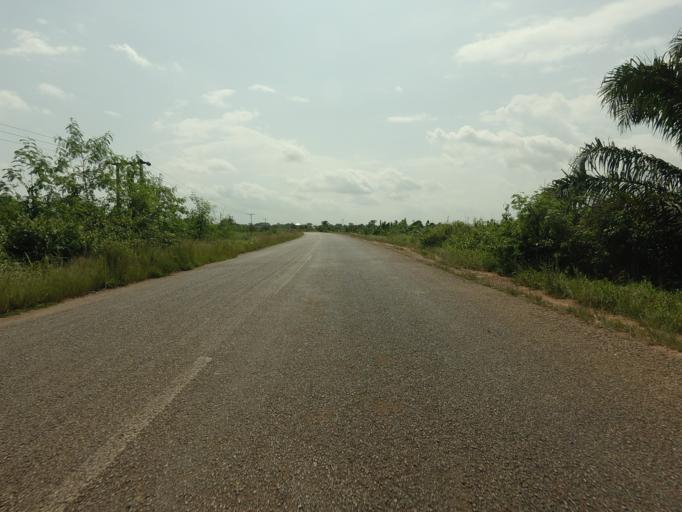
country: TG
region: Maritime
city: Lome
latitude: 6.2463
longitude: 0.9793
